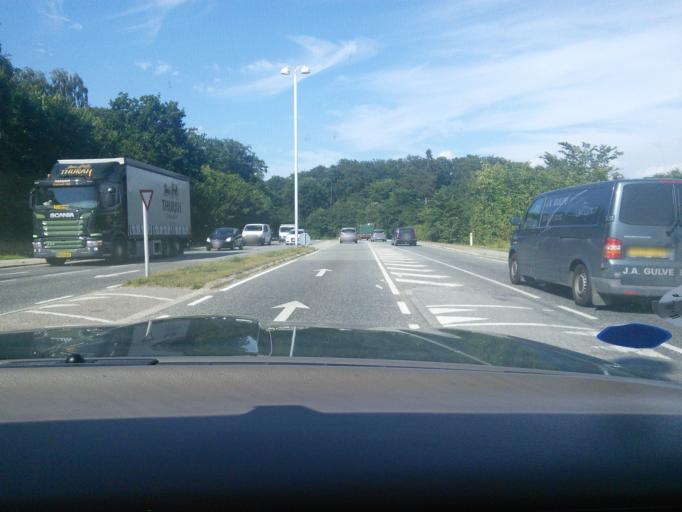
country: DK
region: Capital Region
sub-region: Halsnaes Kommune
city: Frederiksvaerk
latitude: 55.9693
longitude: 12.0301
